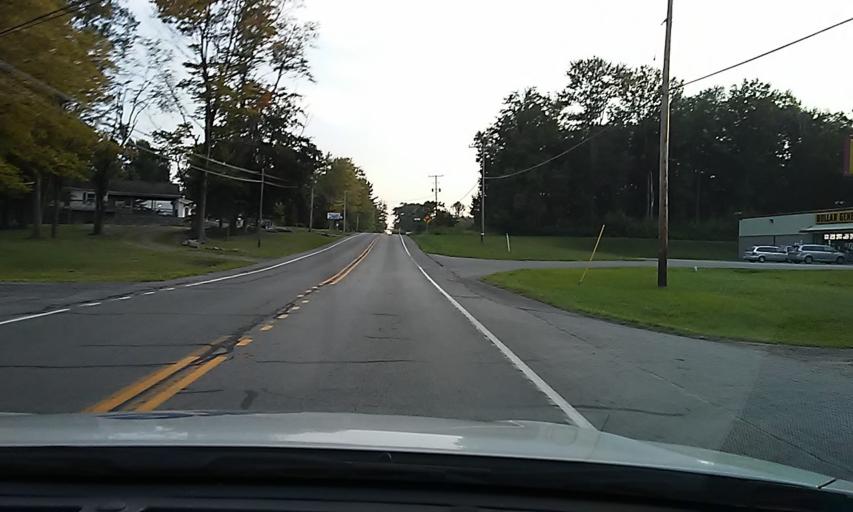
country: US
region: Pennsylvania
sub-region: Forest County
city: Marienville
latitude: 41.4620
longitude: -79.1333
